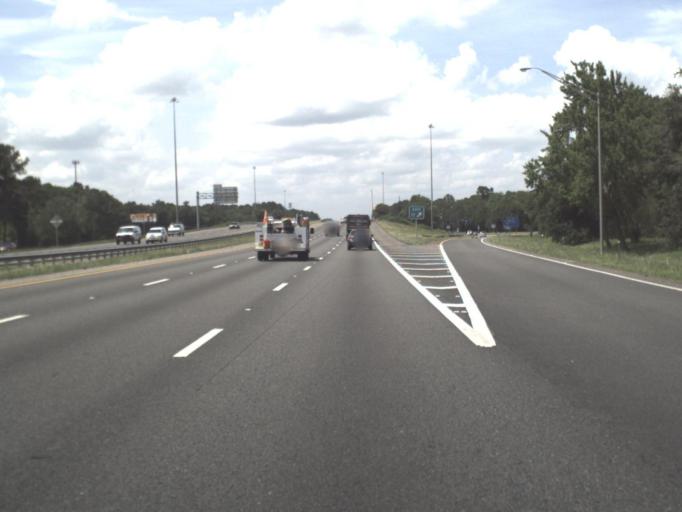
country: US
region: Florida
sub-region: Clay County
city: Bellair-Meadowbrook Terrace
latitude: 30.2662
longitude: -81.7657
